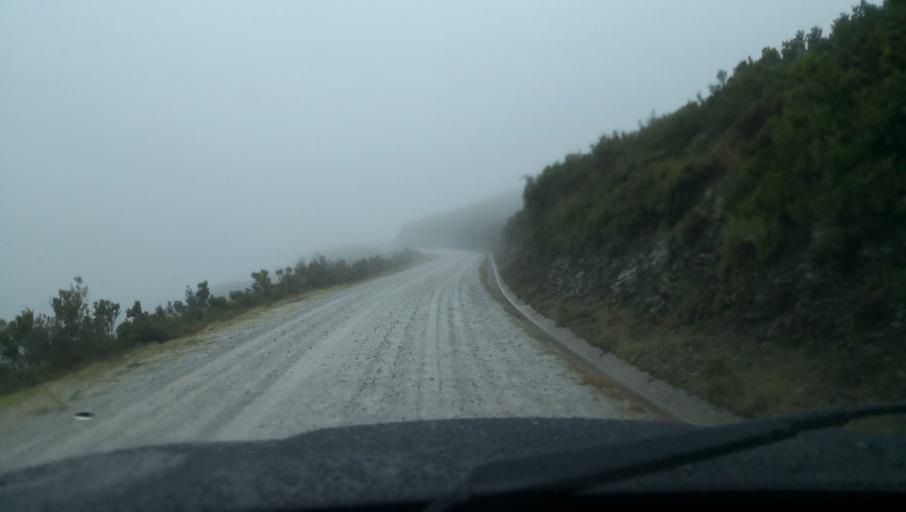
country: PT
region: Vila Real
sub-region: Vila Real
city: Vila Real
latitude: 41.3230
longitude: -7.8616
